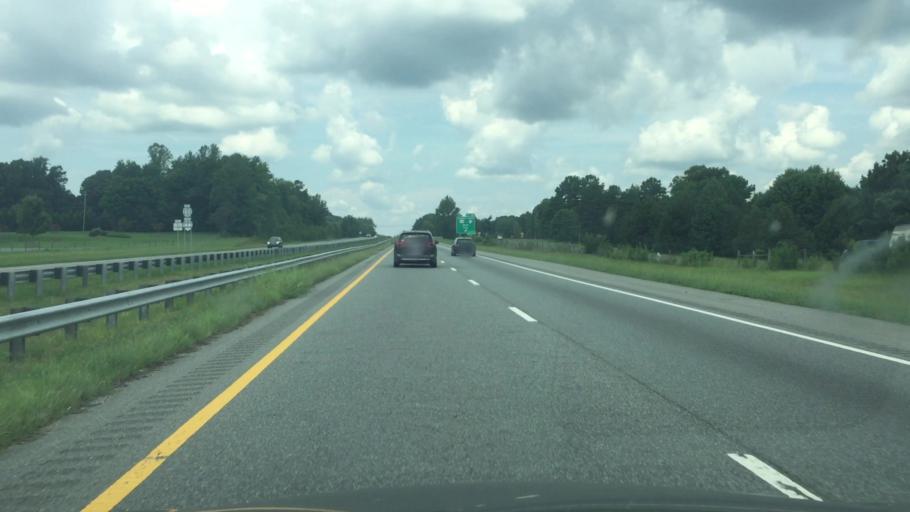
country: US
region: North Carolina
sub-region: Randolph County
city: Asheboro
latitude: 35.6152
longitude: -79.8212
